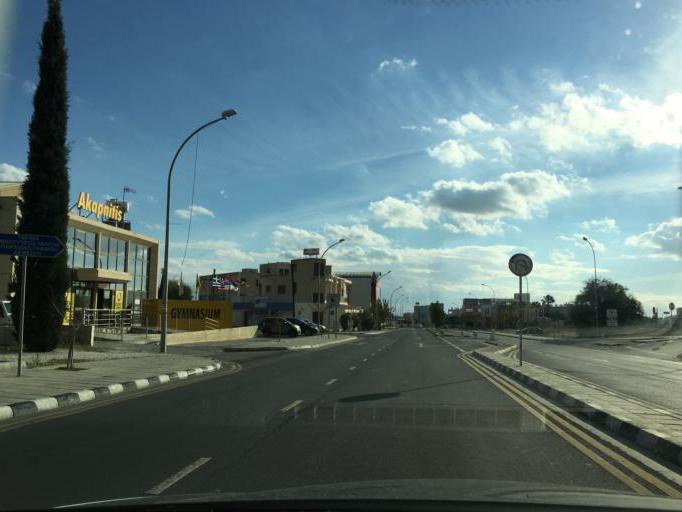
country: CY
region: Limassol
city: Limassol
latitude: 34.7049
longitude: 33.0606
